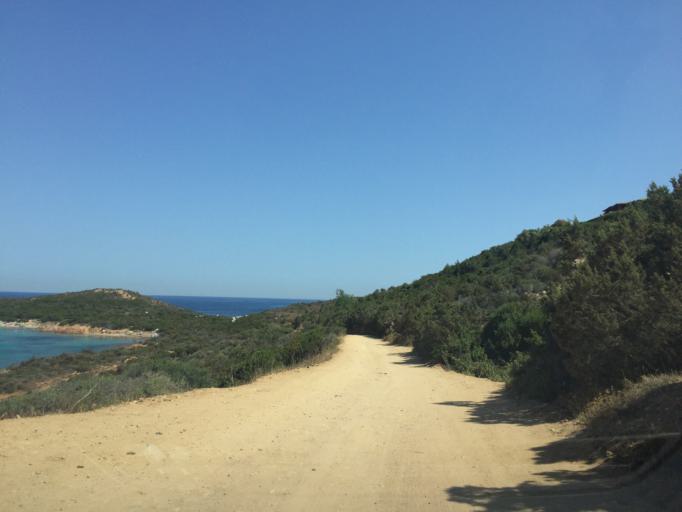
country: IT
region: Sardinia
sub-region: Provincia di Olbia-Tempio
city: San Teodoro
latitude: 40.8413
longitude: 9.7167
